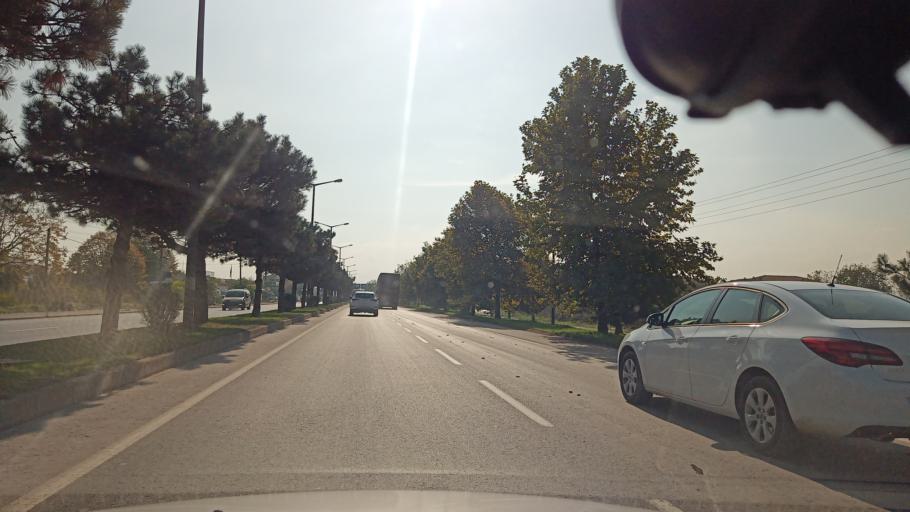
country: TR
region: Sakarya
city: Adapazari
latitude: 40.8061
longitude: 30.4057
